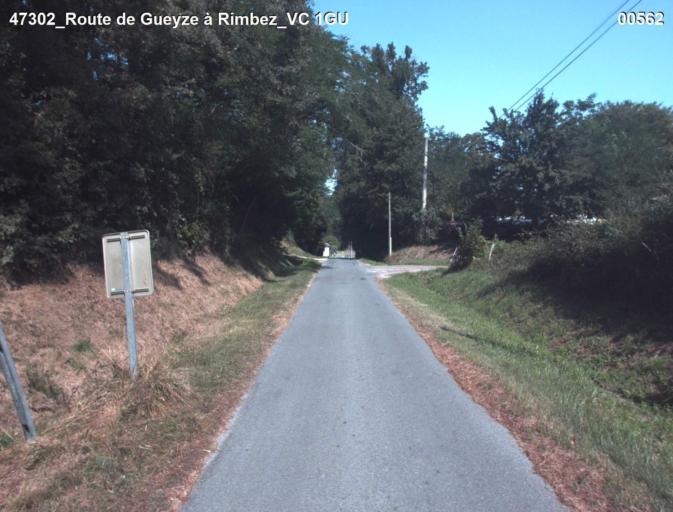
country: FR
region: Midi-Pyrenees
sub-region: Departement du Gers
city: Montreal
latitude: 44.0438
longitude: 0.1293
